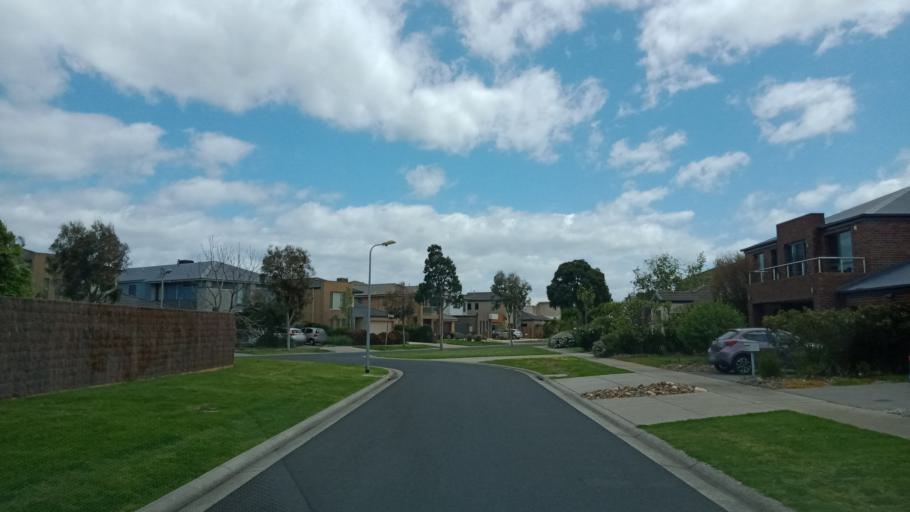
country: AU
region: Victoria
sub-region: Kingston
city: Patterson Lakes
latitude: -38.0601
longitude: 145.1407
